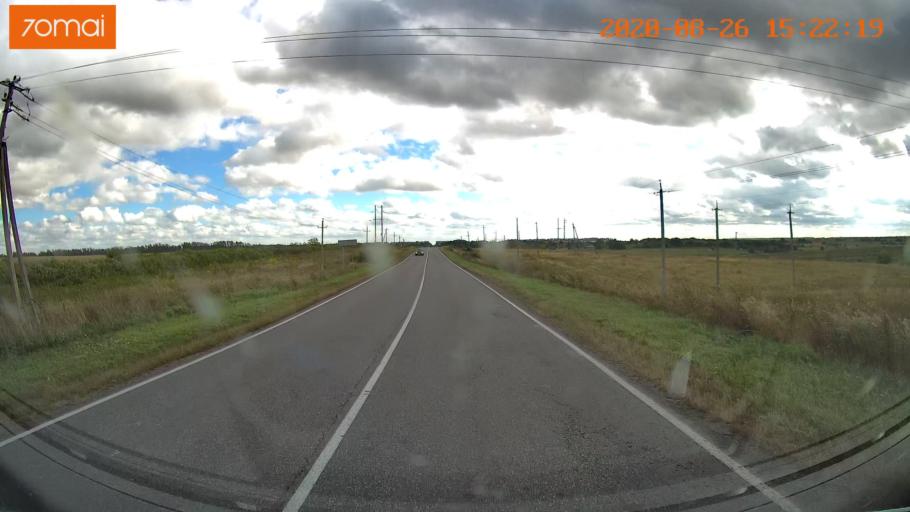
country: RU
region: Tula
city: Severo-Zadonsk
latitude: 54.1333
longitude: 38.4540
